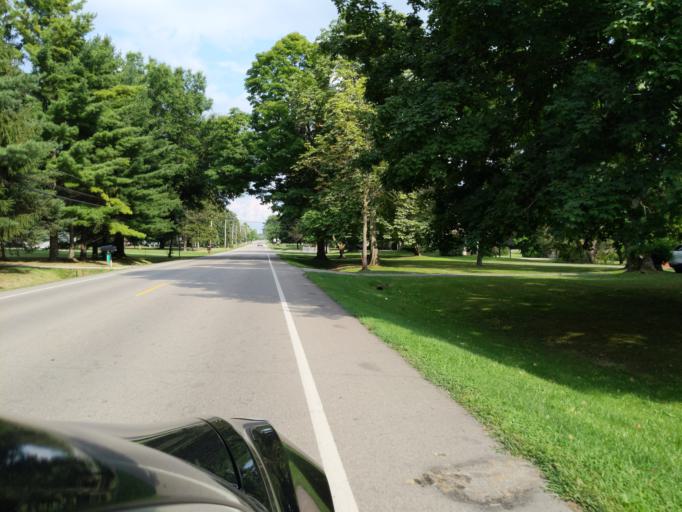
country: US
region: Michigan
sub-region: Clinton County
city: DeWitt
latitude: 42.8344
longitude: -84.5555
